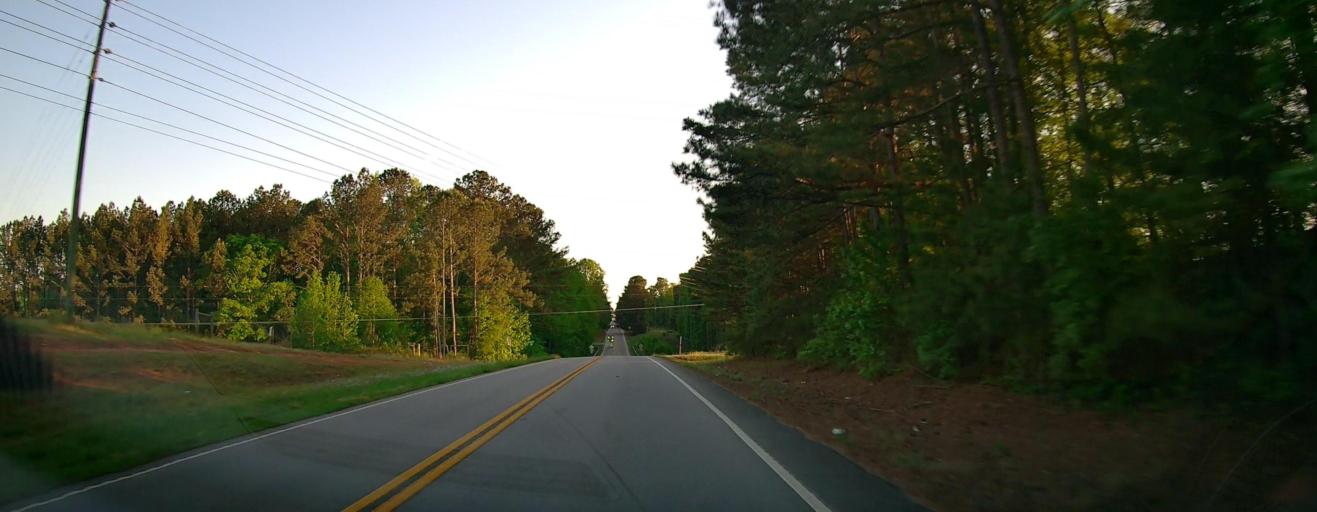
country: US
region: Georgia
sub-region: Newton County
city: Oakwood
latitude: 33.4768
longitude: -83.9622
